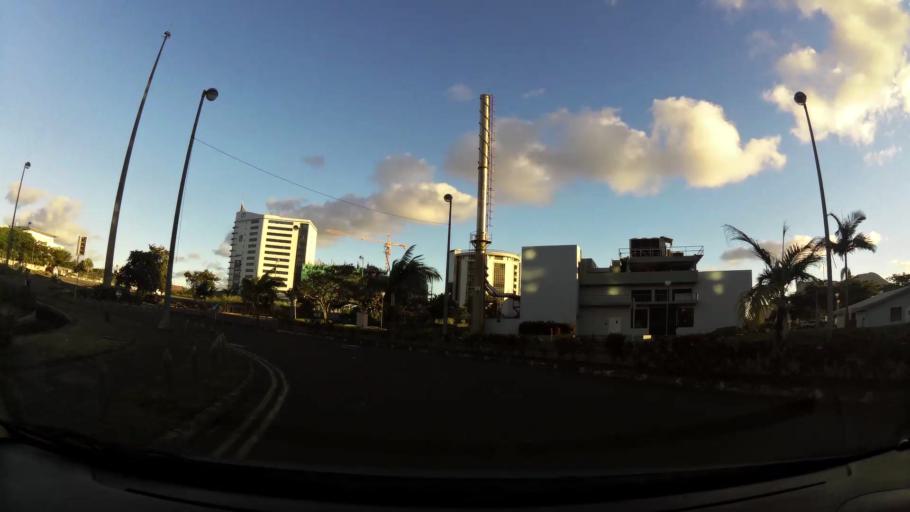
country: MU
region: Plaines Wilhems
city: Ebene
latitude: -20.2454
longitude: 57.4926
